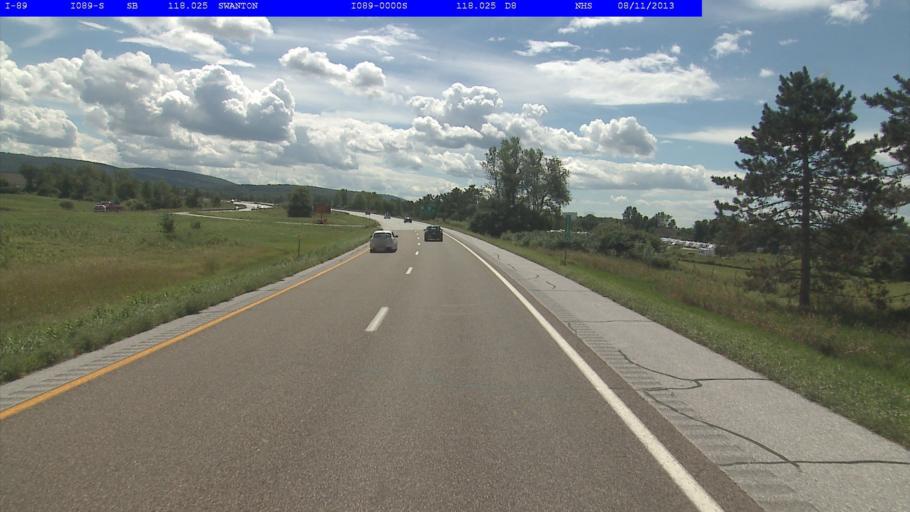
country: US
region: Vermont
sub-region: Franklin County
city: Saint Albans
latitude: 44.8487
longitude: -73.0836
